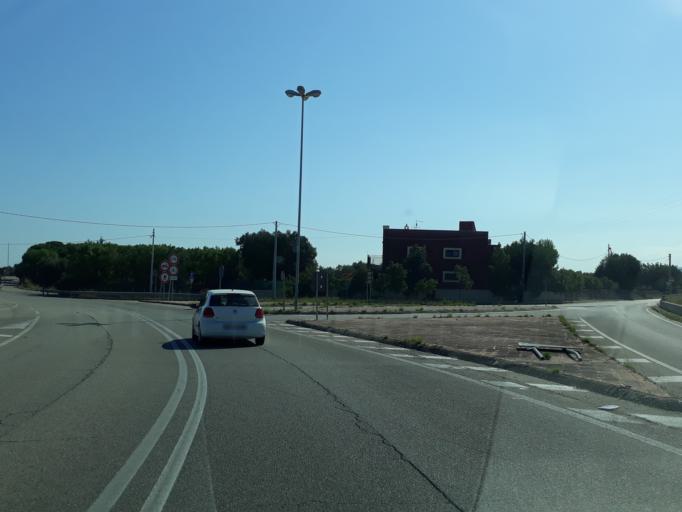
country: IT
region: Apulia
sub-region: Provincia di Bari
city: Monopoli
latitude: 40.9193
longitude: 17.3161
